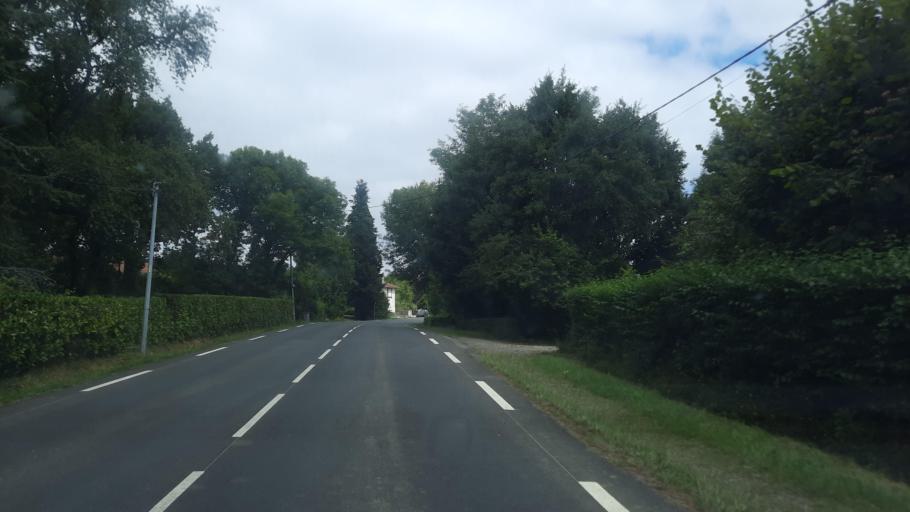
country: FR
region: Midi-Pyrenees
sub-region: Departement des Hautes-Pyrenees
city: Orleix
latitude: 43.2647
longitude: 0.1550
